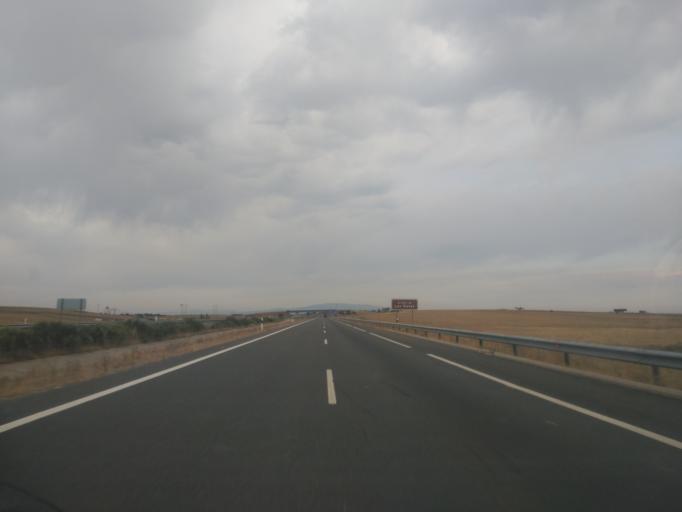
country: ES
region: Castille and Leon
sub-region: Provincia de Salamanca
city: Montejo
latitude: 40.6450
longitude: -5.6305
